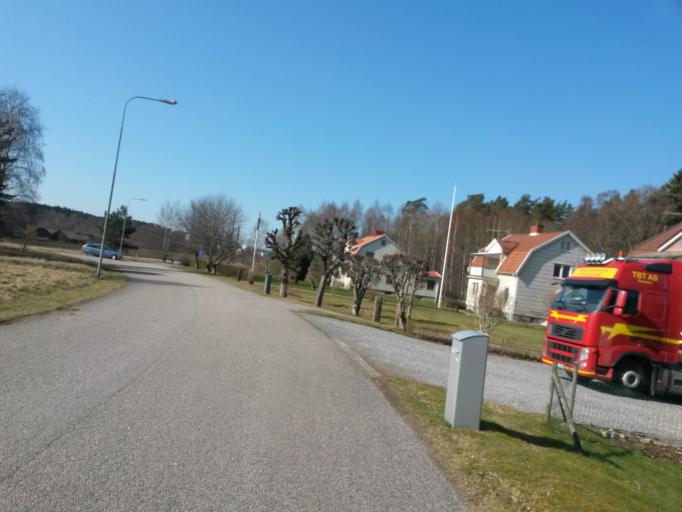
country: SE
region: Vaestra Goetaland
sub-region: Vargarda Kommun
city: Vargarda
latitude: 58.0238
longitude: 12.7981
